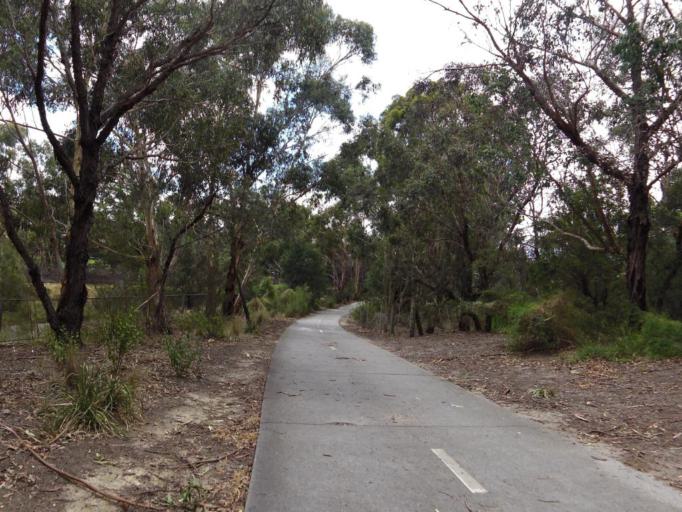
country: AU
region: Victoria
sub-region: Monash
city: Ashwood
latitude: -37.8561
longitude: 145.1041
